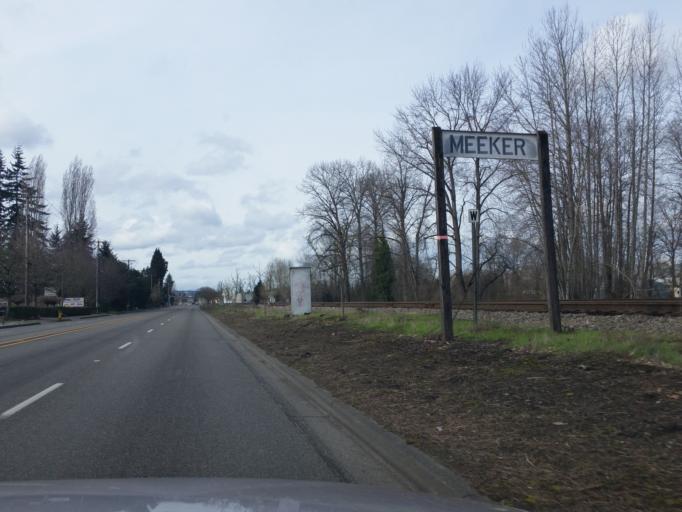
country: US
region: Washington
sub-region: Pierce County
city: North Puyallup
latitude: 47.1878
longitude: -122.2687
